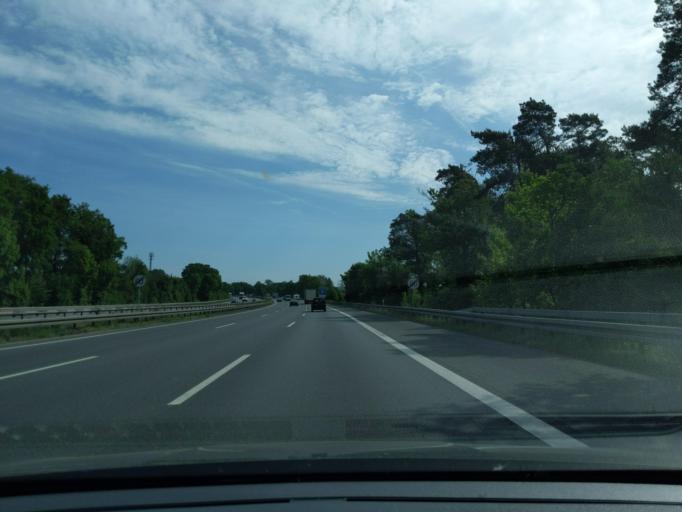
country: DE
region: North Rhine-Westphalia
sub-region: Regierungsbezirk Detmold
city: Verl
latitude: 51.9050
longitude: 8.5009
